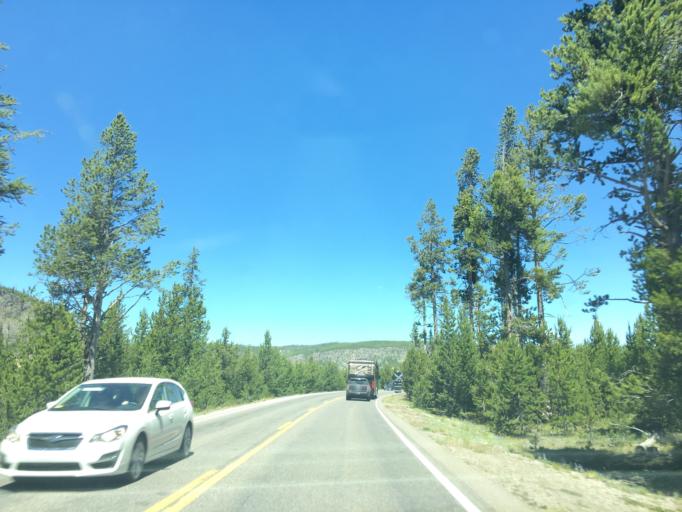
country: US
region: Montana
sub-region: Gallatin County
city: West Yellowstone
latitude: 44.4699
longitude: -110.8572
